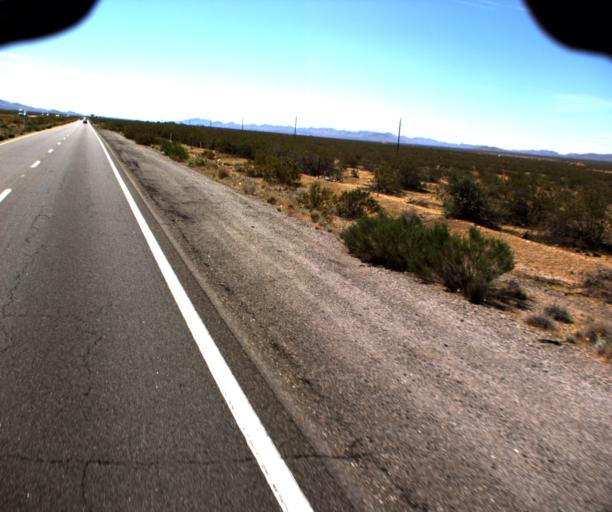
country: US
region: Arizona
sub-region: Mohave County
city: Dolan Springs
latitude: 35.5796
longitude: -114.3873
